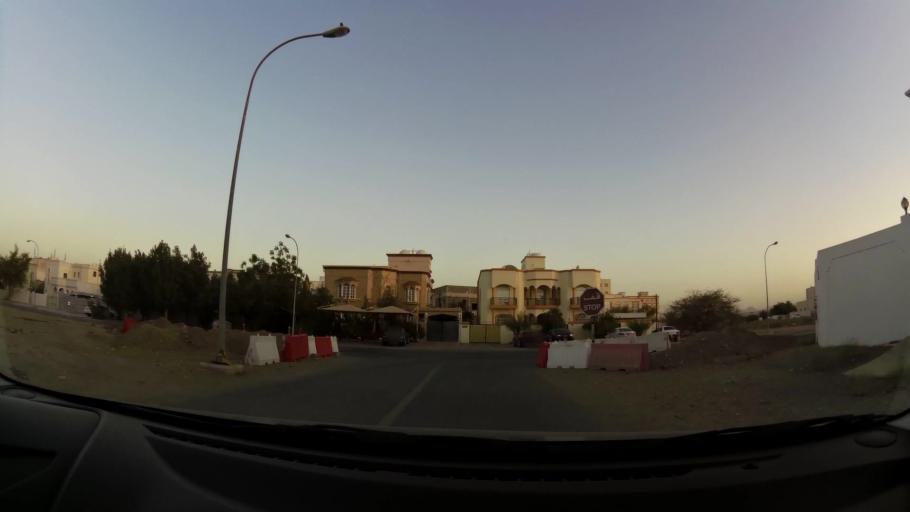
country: OM
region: Muhafazat Masqat
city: As Sib al Jadidah
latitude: 23.5952
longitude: 58.2339
